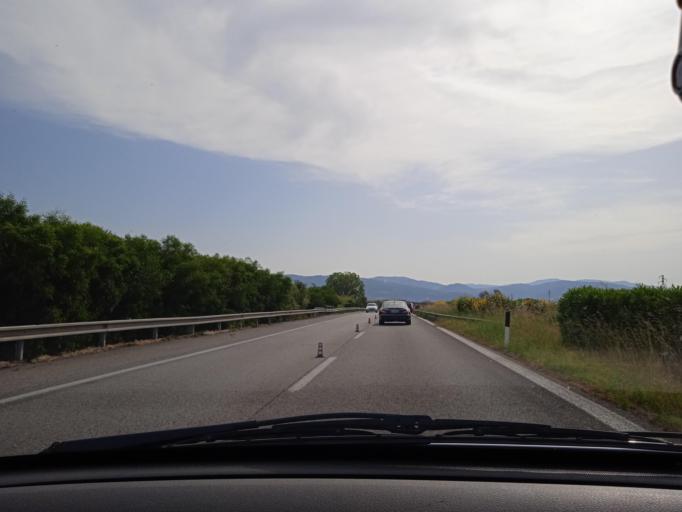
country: IT
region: Sicily
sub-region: Messina
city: Terme
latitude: 38.1378
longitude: 15.1519
